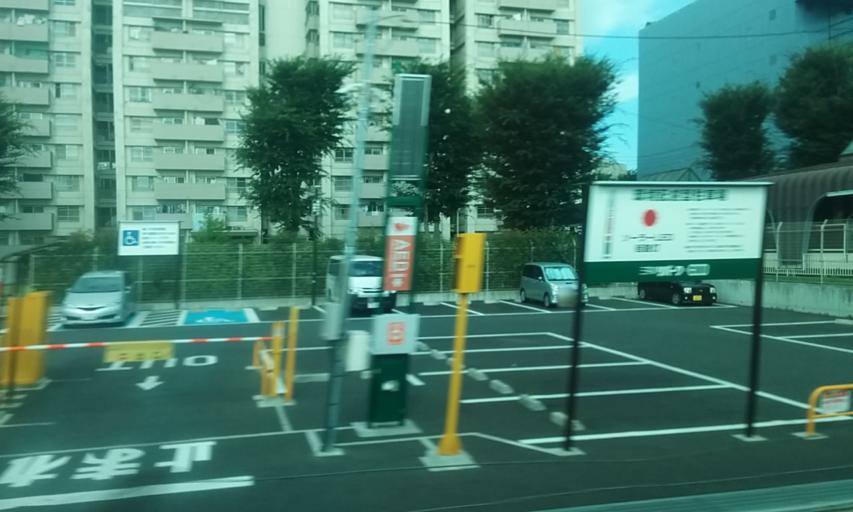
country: JP
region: Saitama
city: Yono
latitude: 35.8785
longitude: 139.6413
